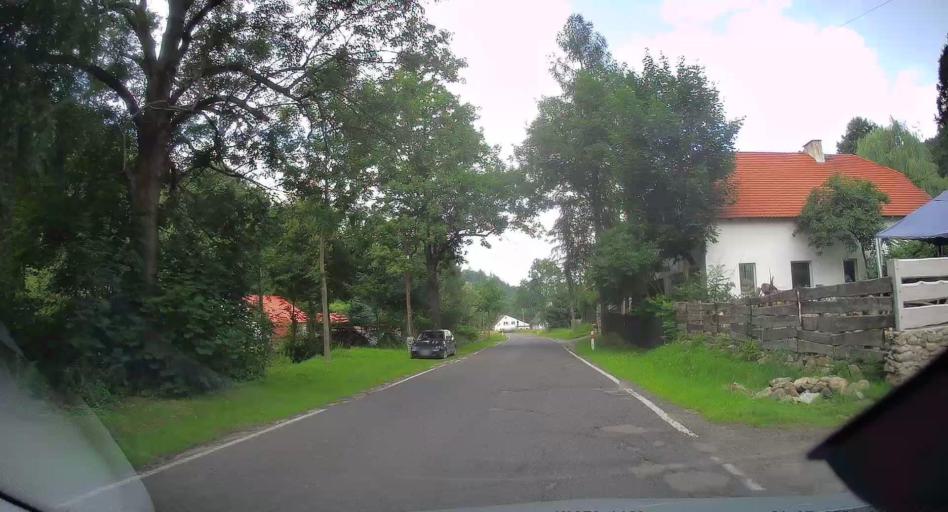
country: PL
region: Lower Silesian Voivodeship
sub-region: Powiat walbrzyski
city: Walim
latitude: 50.7163
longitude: 16.4257
